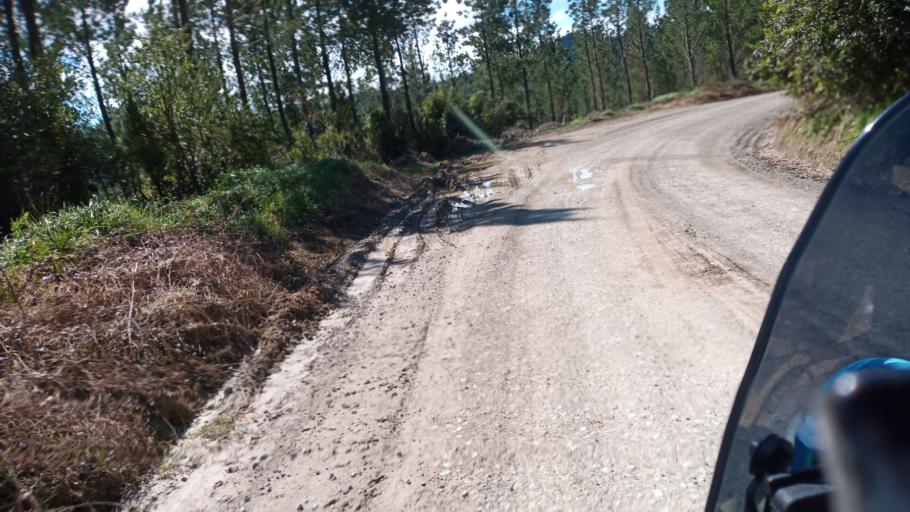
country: NZ
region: Gisborne
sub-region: Gisborne District
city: Gisborne
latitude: -38.9074
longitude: 177.8092
